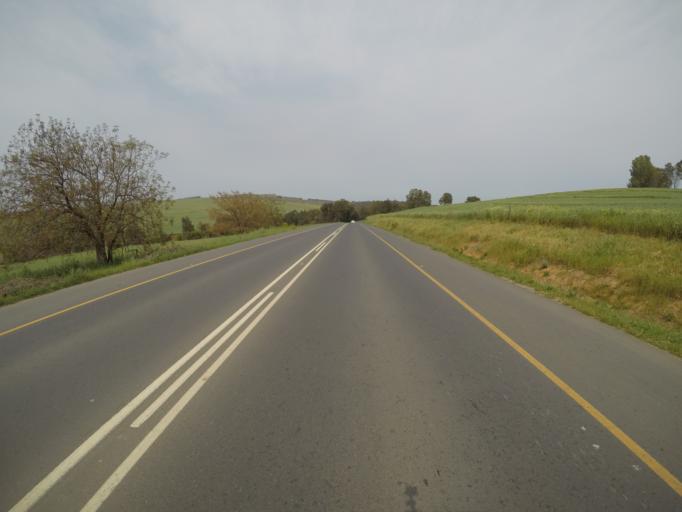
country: ZA
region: Western Cape
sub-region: West Coast District Municipality
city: Malmesbury
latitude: -33.4552
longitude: 18.7479
